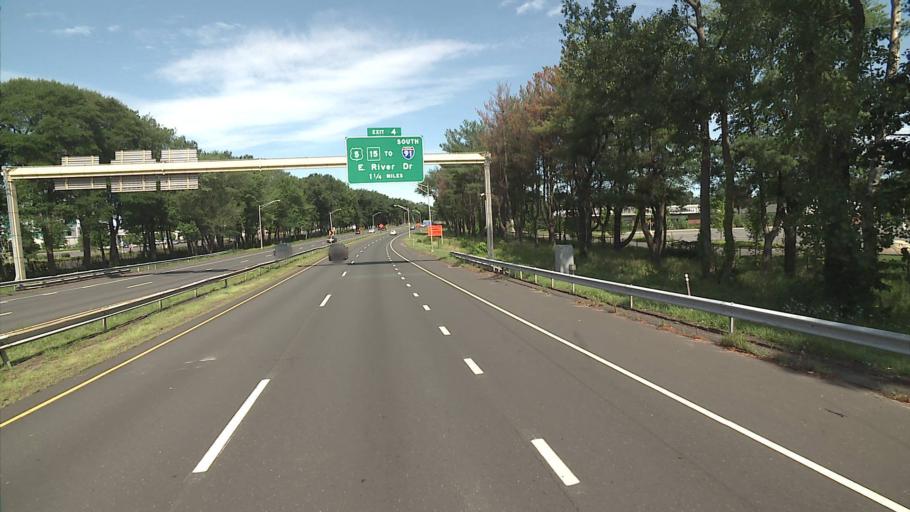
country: US
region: Connecticut
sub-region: Hartford County
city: Wethersfield
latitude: 41.7430
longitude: -72.6370
